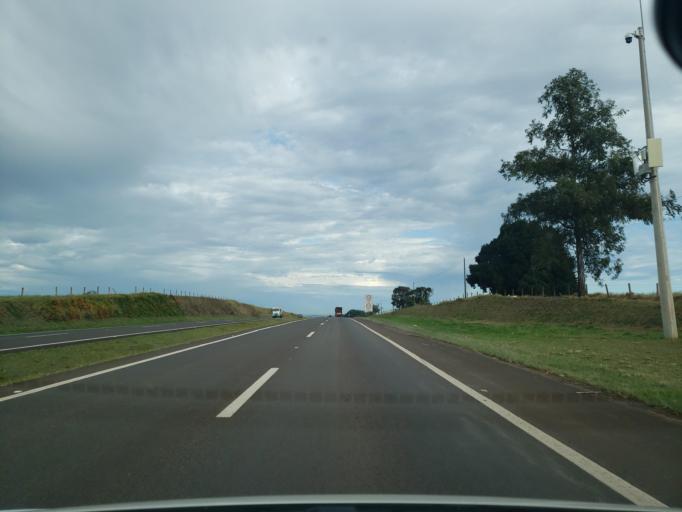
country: BR
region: Sao Paulo
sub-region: Jau
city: Jau
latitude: -22.2665
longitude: -48.4487
